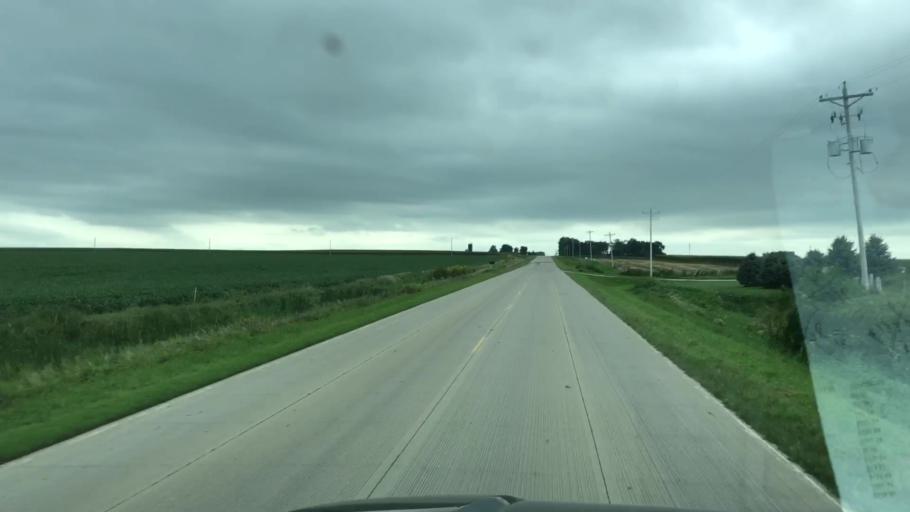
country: US
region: Iowa
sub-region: Sioux County
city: Alton
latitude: 43.1027
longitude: -95.9785
